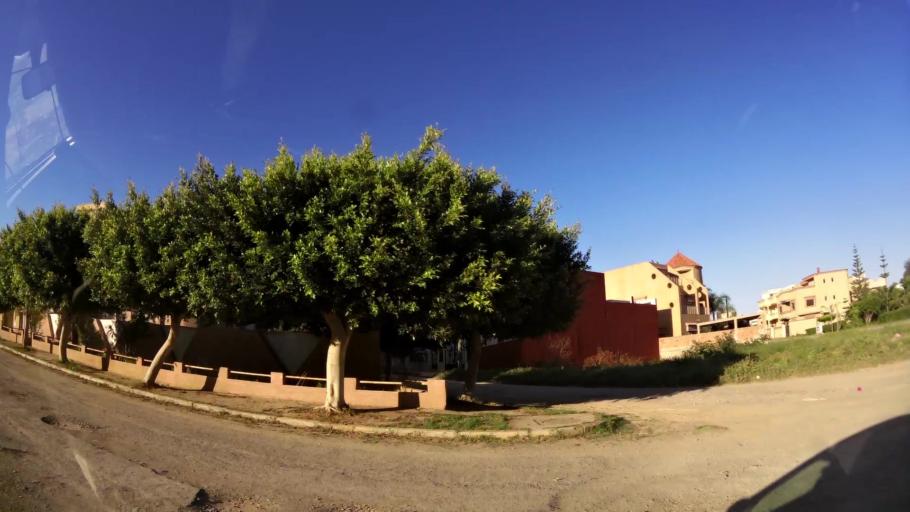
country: MA
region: Oriental
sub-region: Berkane-Taourirt
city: Madagh
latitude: 35.0870
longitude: -2.2472
